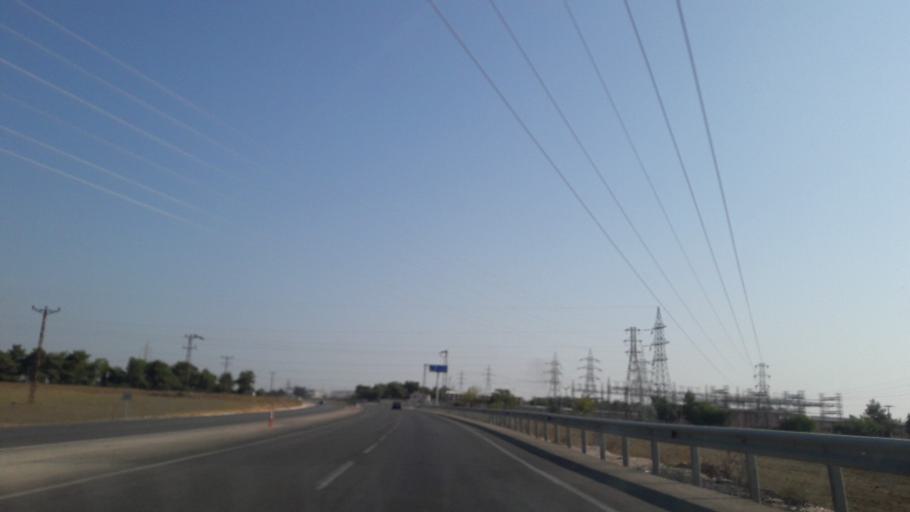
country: TR
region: Adana
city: Yakapinar
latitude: 37.0978
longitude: 35.5050
